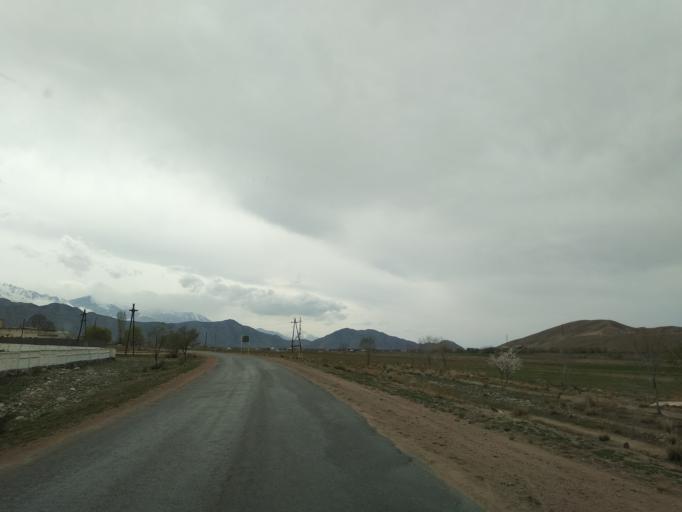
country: KG
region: Ysyk-Koel
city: Bokombayevskoye
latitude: 42.1257
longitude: 76.9915
